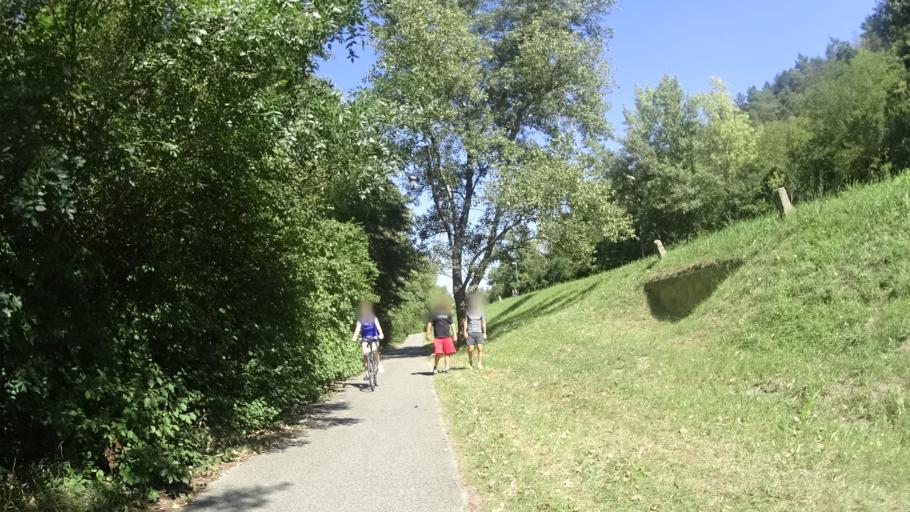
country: AT
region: Lower Austria
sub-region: Politischer Bezirk Bruck an der Leitha
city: Hainburg an der Donau
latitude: 48.1841
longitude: 16.9782
